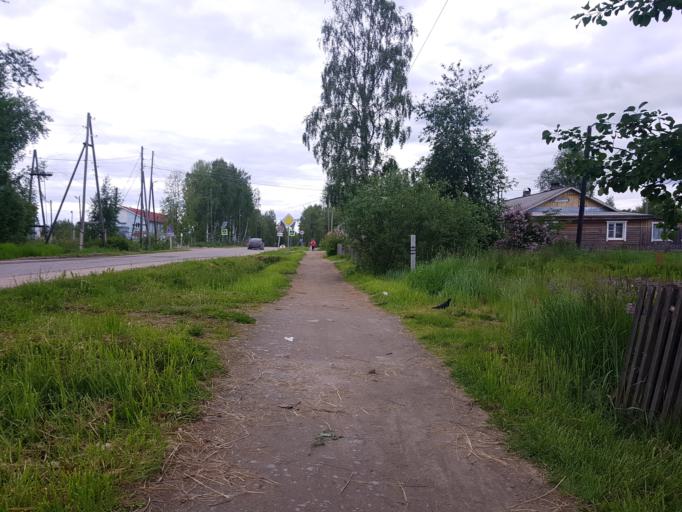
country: RU
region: Republic of Karelia
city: Kalevala
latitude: 65.2011
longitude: 31.1768
